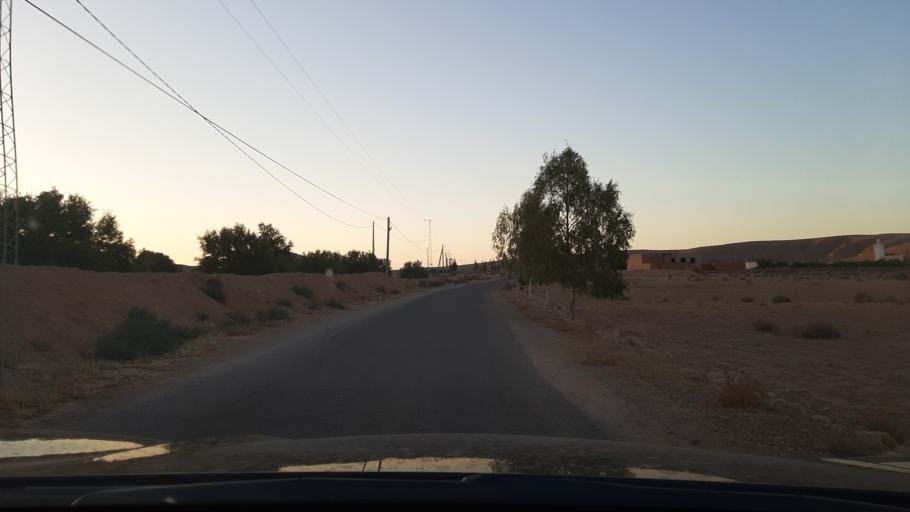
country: TN
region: Qabis
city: Matmata
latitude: 33.5662
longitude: 10.1785
